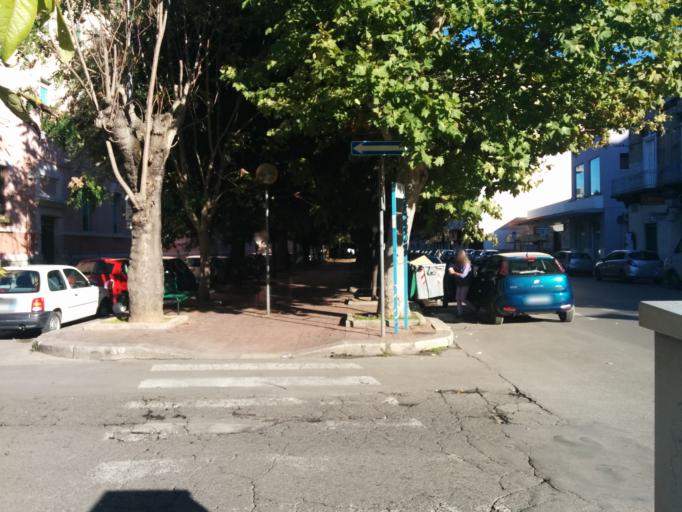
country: IT
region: Apulia
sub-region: Provincia di Taranto
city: Taranto
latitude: 40.4661
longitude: 17.2699
